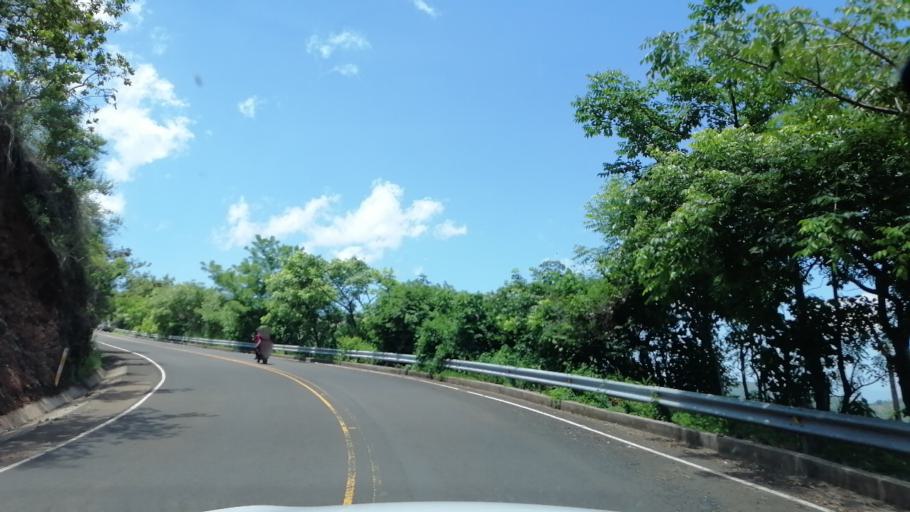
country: SV
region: San Miguel
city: Ciudad Barrios
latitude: 13.7913
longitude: -88.2896
